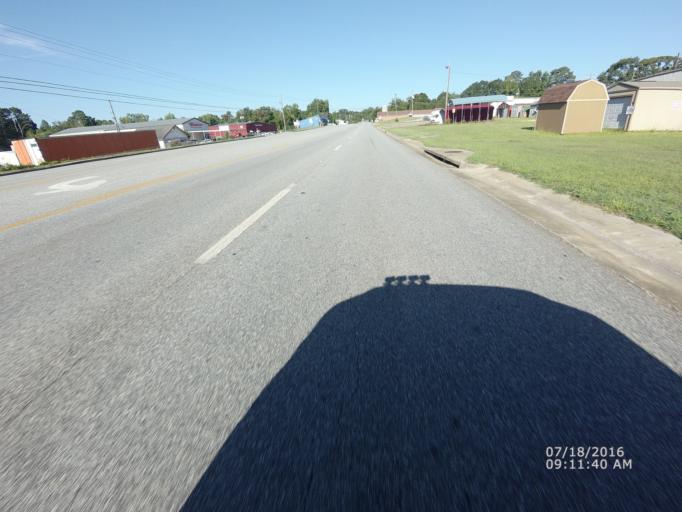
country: US
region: Alabama
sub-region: Chambers County
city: Huguley
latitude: 32.8484
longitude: -85.2137
